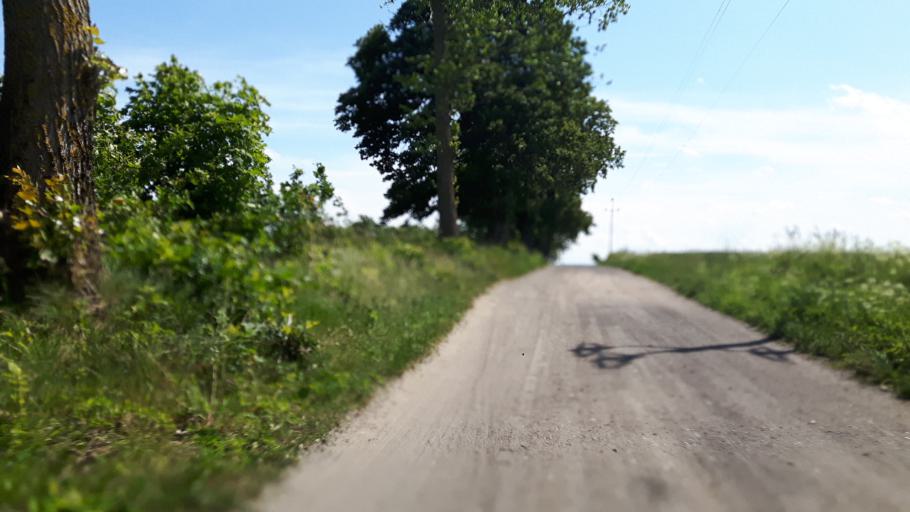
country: PL
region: Pomeranian Voivodeship
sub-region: Powiat wejherowski
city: Gniewino
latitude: 54.7296
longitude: 17.9552
